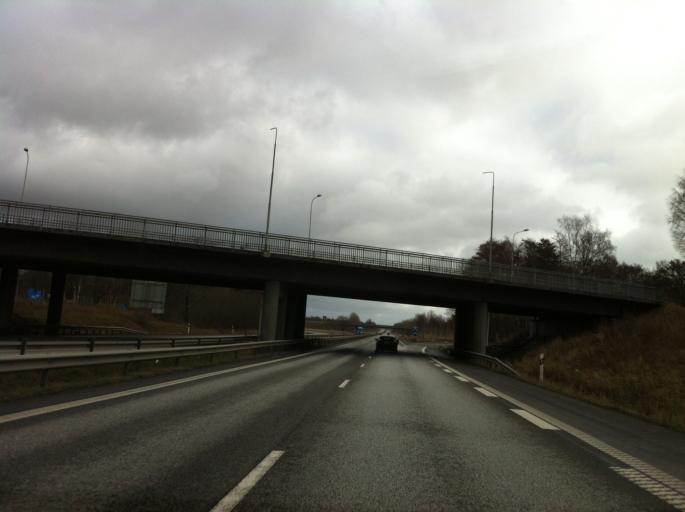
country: SE
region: Skane
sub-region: Kristianstads Kommun
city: Kristianstad
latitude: 56.0263
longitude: 14.0945
